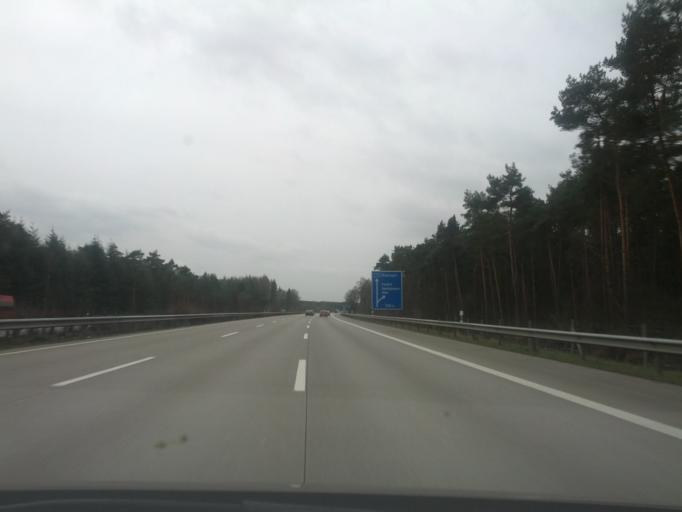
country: DE
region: Lower Saxony
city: Egestorf
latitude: 53.1700
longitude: 10.0740
